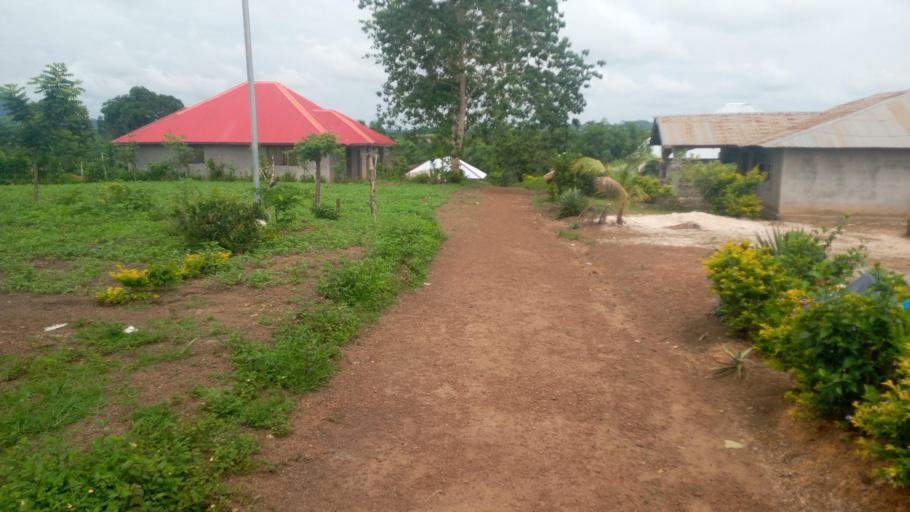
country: SL
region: Southern Province
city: Mogbwemo
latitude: 7.7827
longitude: -12.3019
